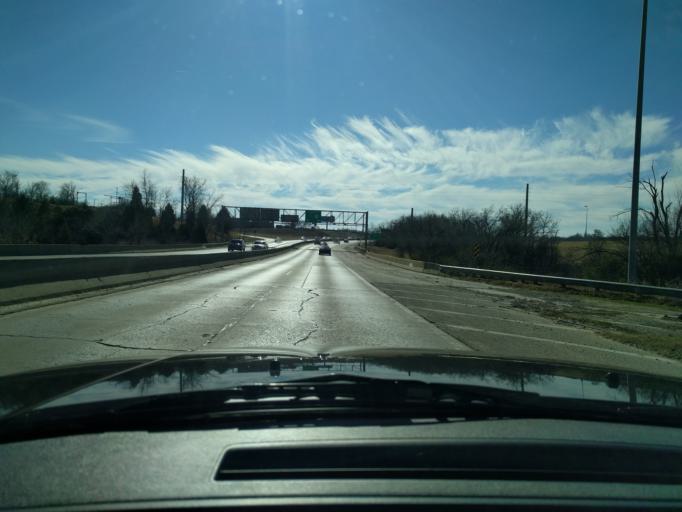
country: US
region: Oklahoma
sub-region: Oklahoma County
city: Nichols Hills
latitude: 35.5279
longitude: -97.5144
